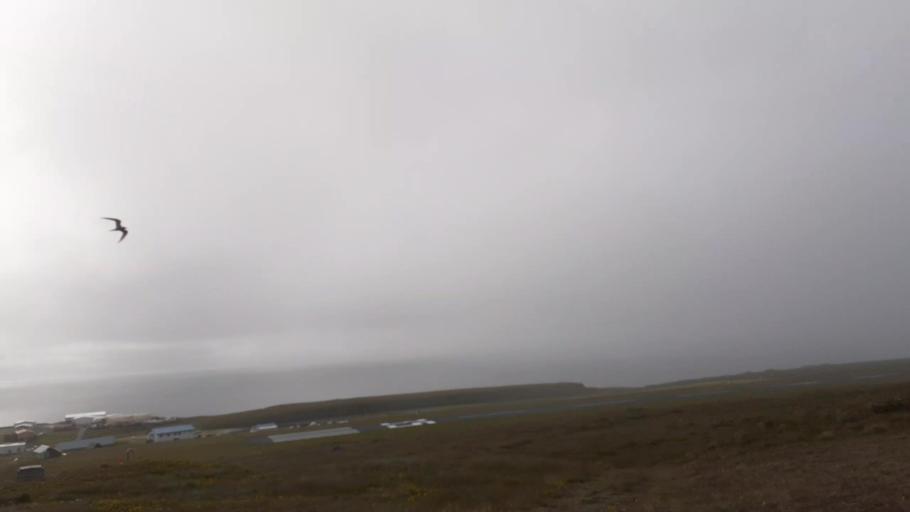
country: IS
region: Northeast
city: Dalvik
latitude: 66.5424
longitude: -18.0073
